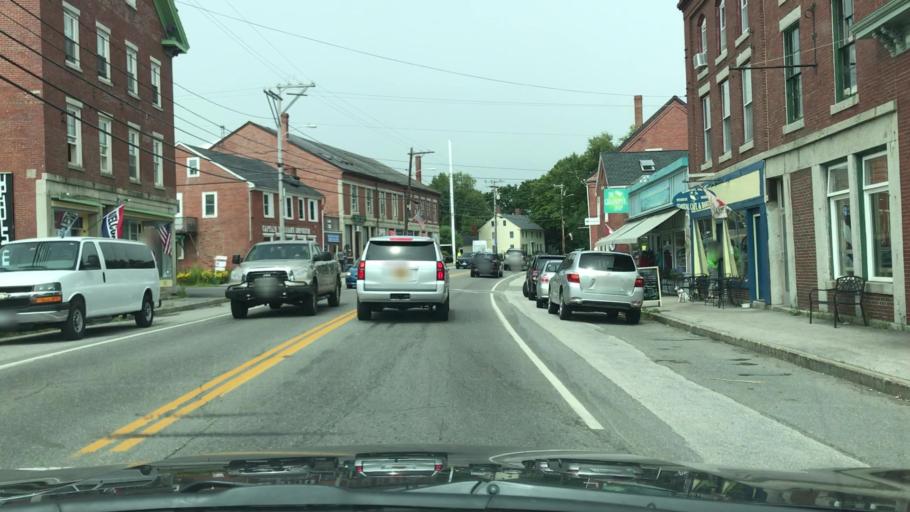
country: US
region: Maine
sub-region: Waldo County
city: Stockton Springs
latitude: 44.4582
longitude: -68.9260
